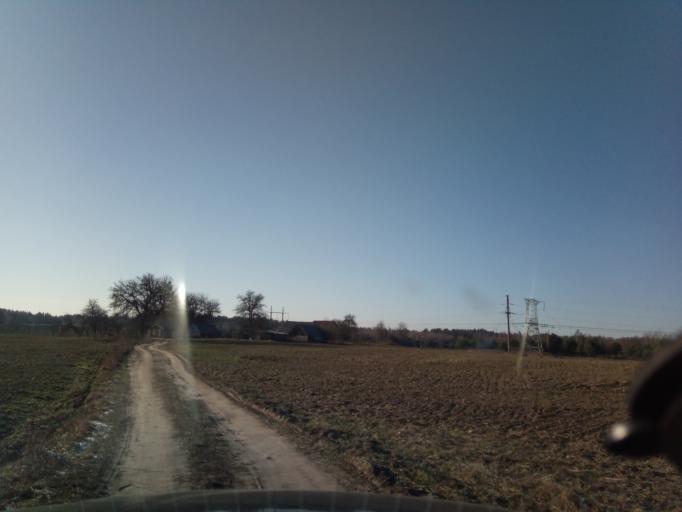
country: LT
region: Alytaus apskritis
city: Druskininkai
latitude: 53.9837
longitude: 23.9002
